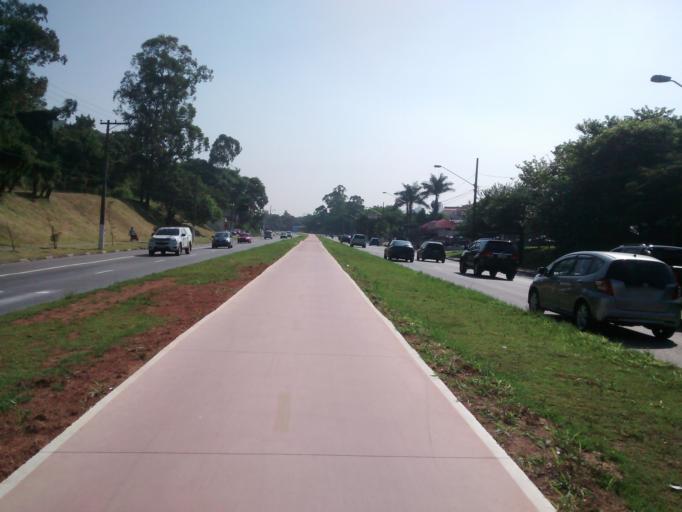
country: BR
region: Sao Paulo
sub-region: Taboao Da Serra
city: Taboao da Serra
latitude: -23.5951
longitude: -46.7450
